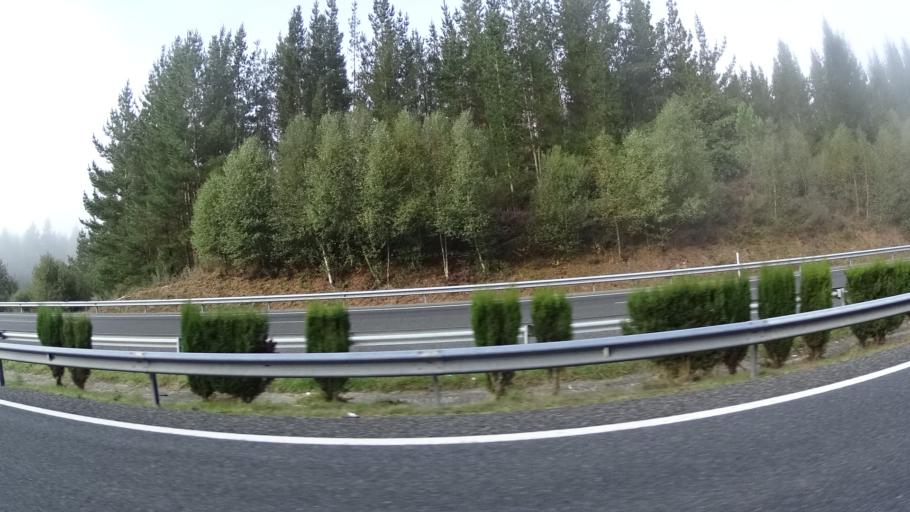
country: ES
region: Galicia
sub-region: Provincia de Lugo
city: O Paramo
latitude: 42.9241
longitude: -7.3569
